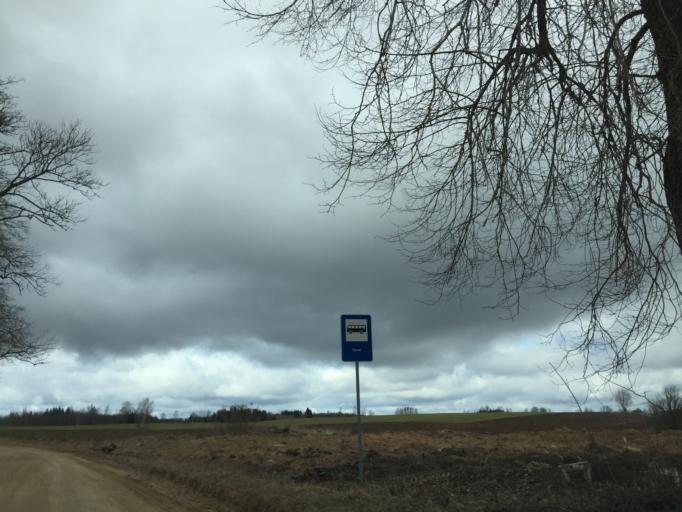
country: LV
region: Ilukste
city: Ilukste
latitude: 56.0729
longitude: 26.0558
